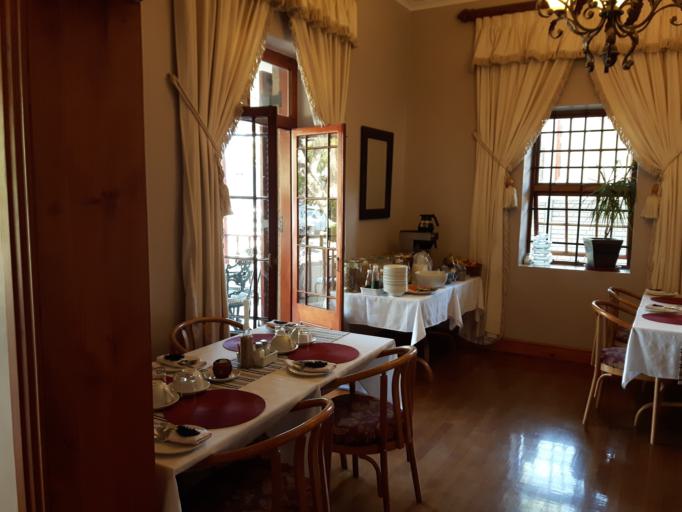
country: ZA
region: Western Cape
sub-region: Eden District Municipality
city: Oudtshoorn
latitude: -33.5853
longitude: 22.2045
